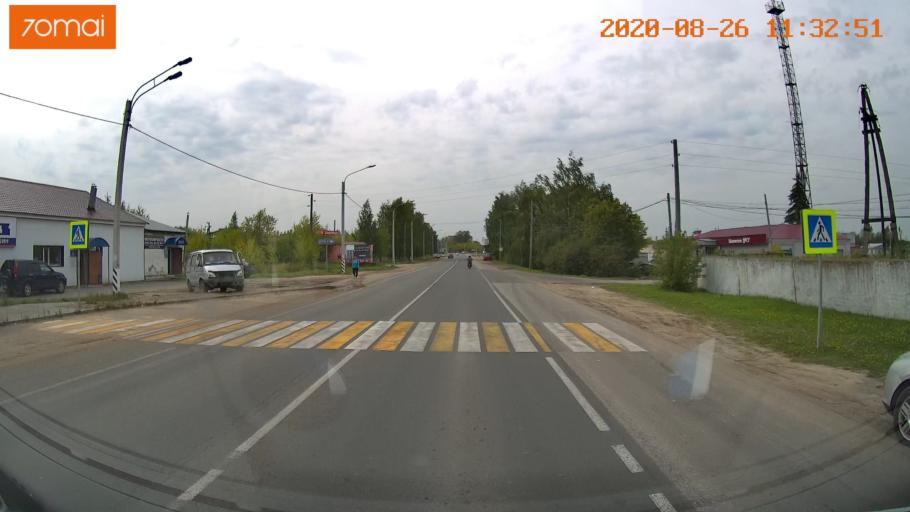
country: RU
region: Rjazan
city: Shilovo
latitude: 54.2998
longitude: 40.8607
